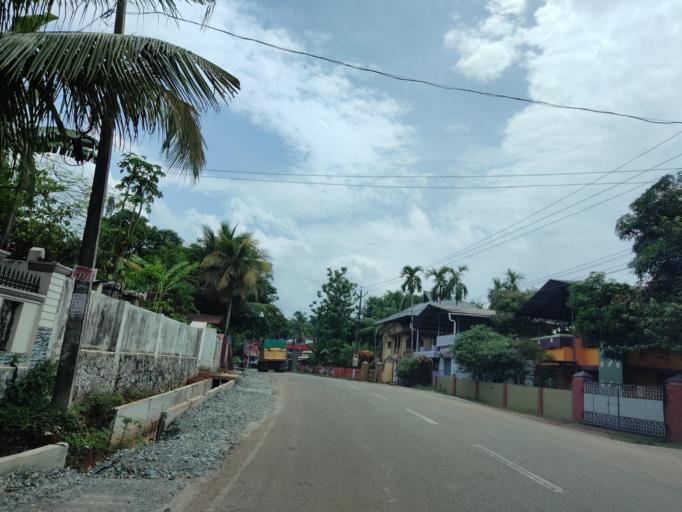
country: IN
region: Kerala
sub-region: Alappuzha
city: Mavelikara
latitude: 9.2272
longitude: 76.6133
